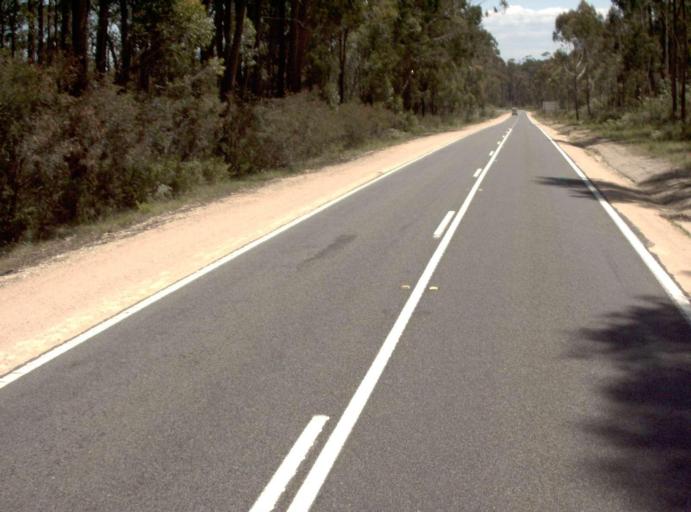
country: AU
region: Victoria
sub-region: East Gippsland
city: Lakes Entrance
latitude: -37.6868
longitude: 148.7571
